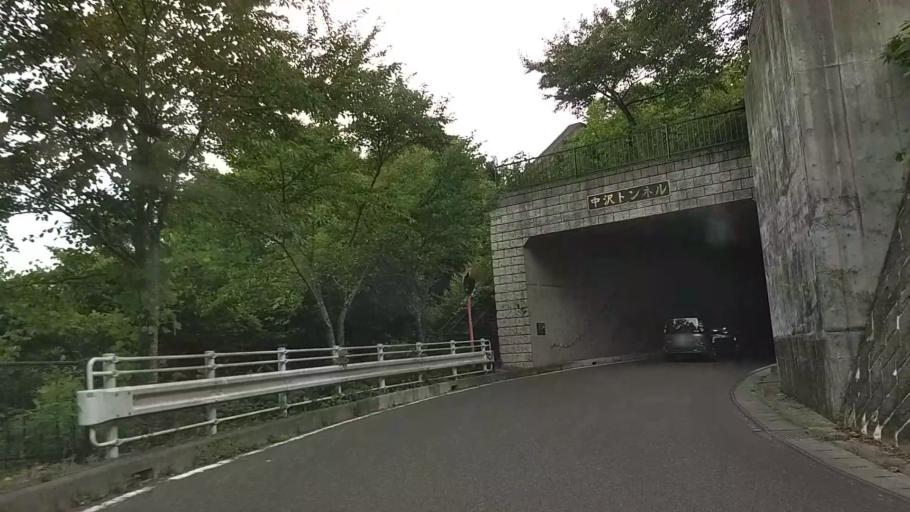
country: JP
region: Yamanashi
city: Uenohara
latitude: 35.5471
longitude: 139.1408
